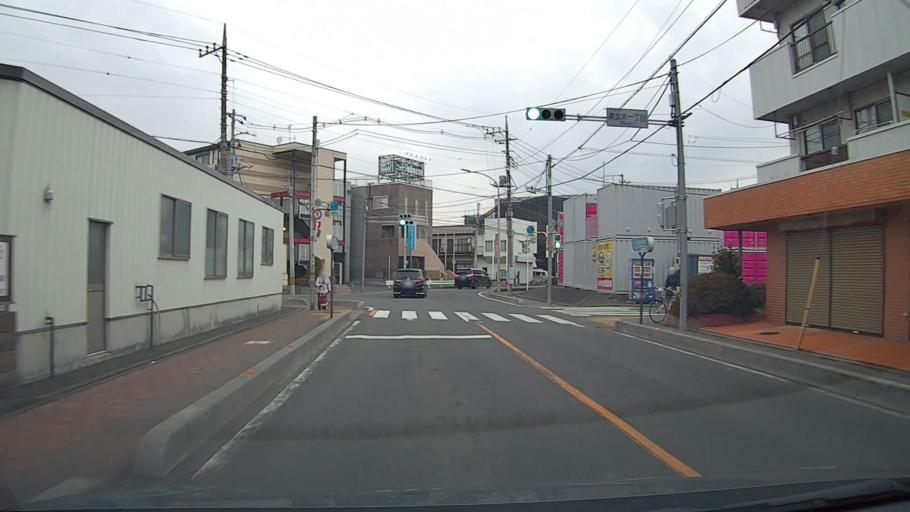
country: JP
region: Saitama
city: Wako
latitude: 35.8301
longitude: 139.6412
